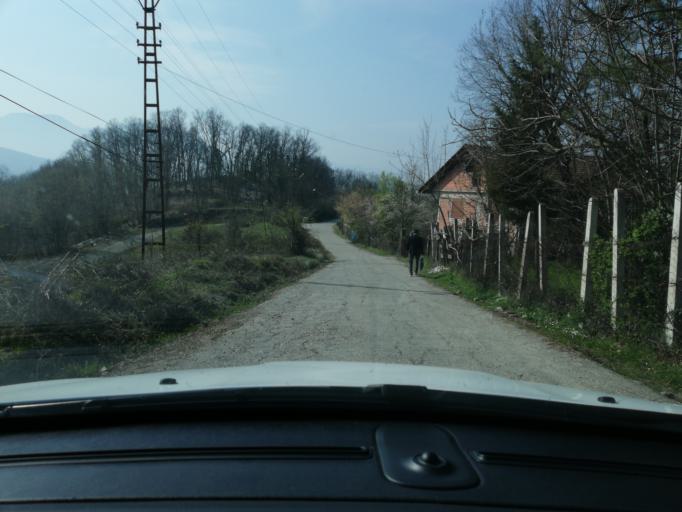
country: TR
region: Karabuk
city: Yenice
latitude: 41.2719
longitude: 32.3543
